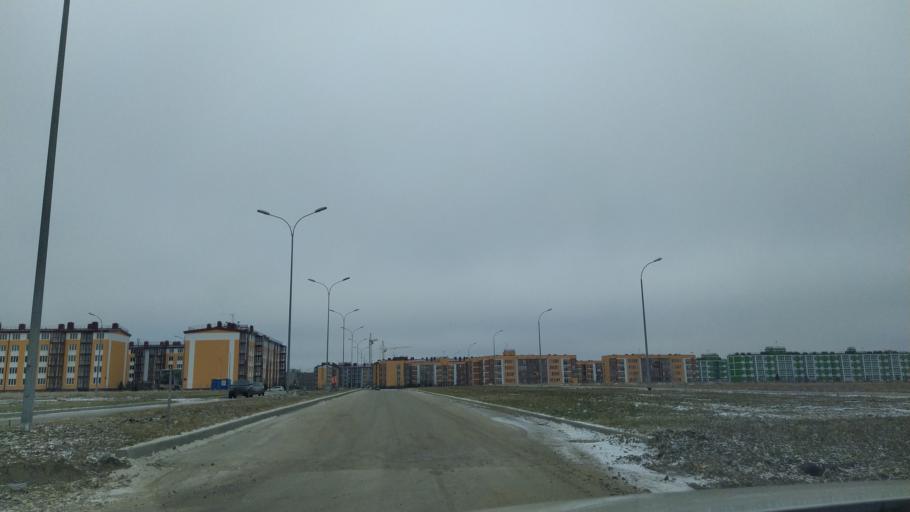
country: RU
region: St.-Petersburg
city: Aleksandrovskaya
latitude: 59.7529
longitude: 30.3613
